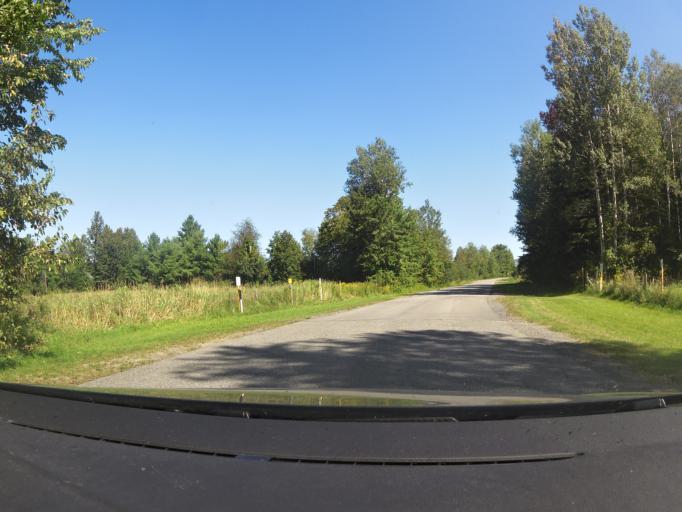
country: CA
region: Ontario
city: Bells Corners
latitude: 45.2786
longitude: -76.0127
